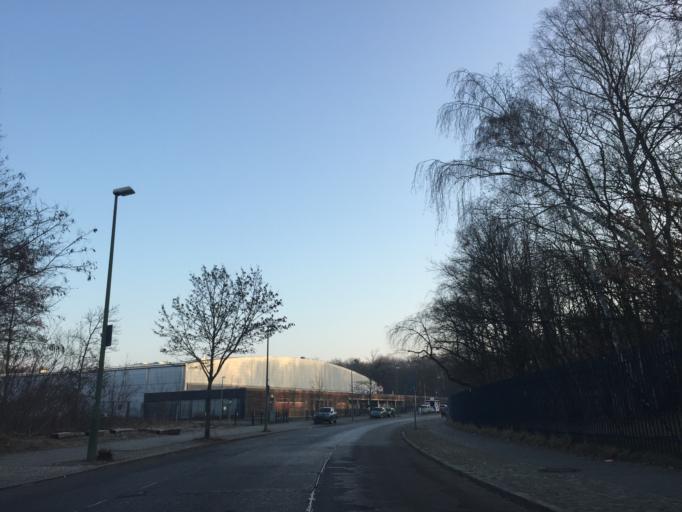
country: DE
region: Berlin
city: Haselhorst
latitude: 52.5132
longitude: 13.2256
